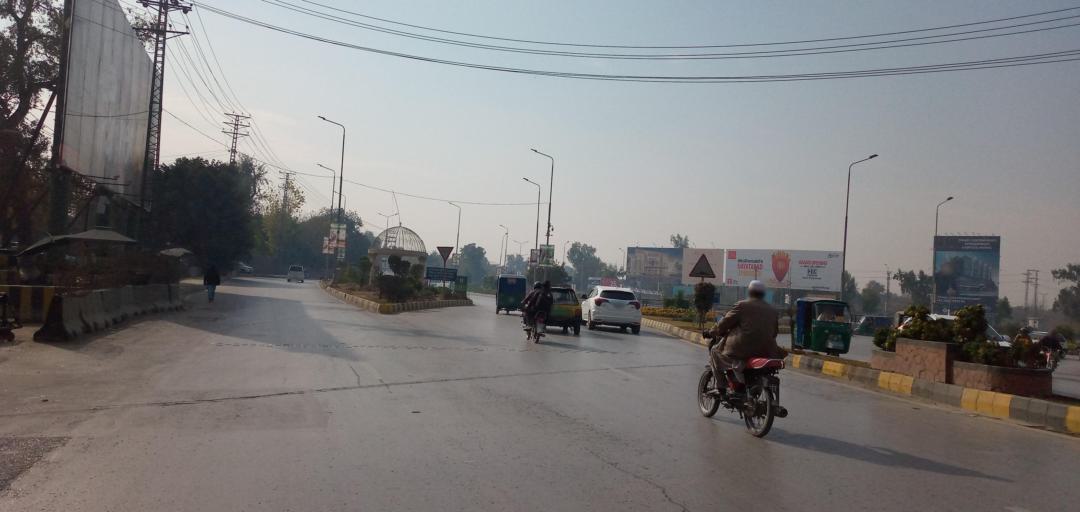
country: PK
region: Khyber Pakhtunkhwa
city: Peshawar
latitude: 34.0064
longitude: 71.5355
